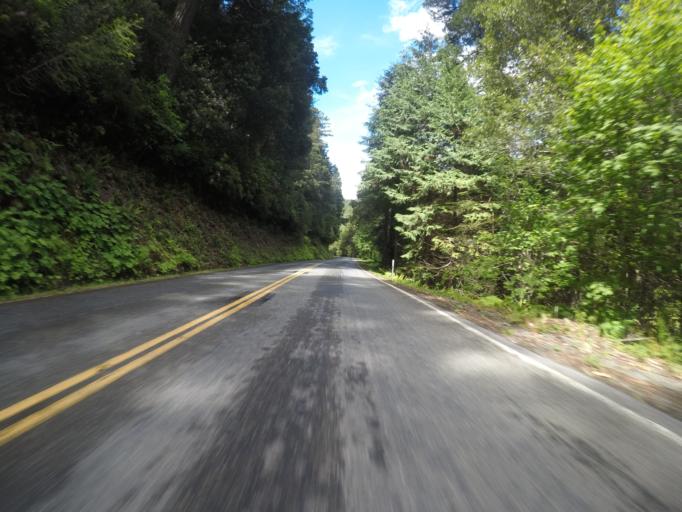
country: US
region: California
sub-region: Del Norte County
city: Bertsch-Oceanview
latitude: 41.7953
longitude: -124.0417
